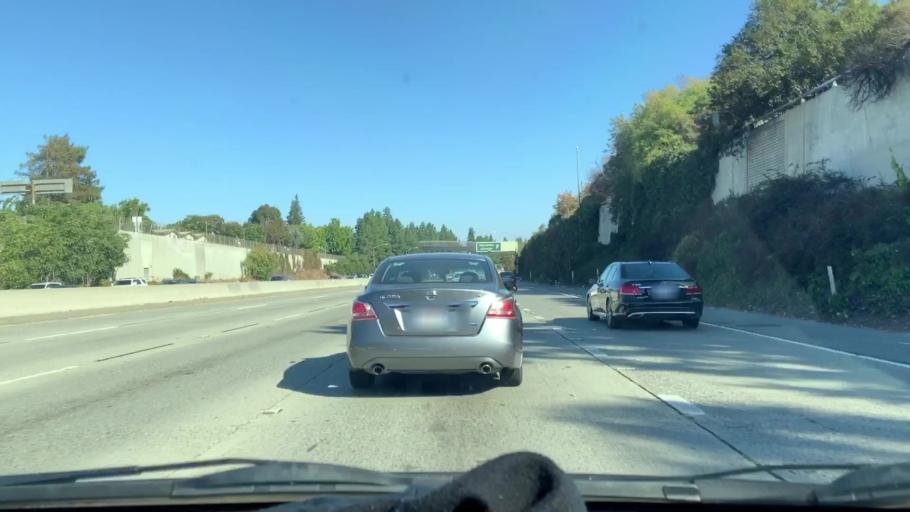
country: US
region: California
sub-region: Santa Clara County
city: Buena Vista
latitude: 37.3167
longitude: -121.9234
